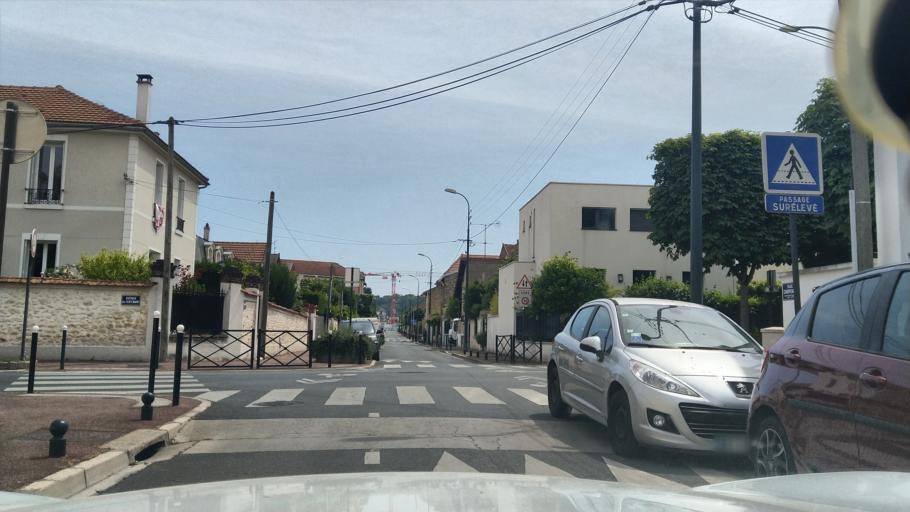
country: FR
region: Ile-de-France
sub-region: Departement du Val-de-Marne
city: Saint-Maur-des-Fosses
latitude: 48.8008
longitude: 2.5091
